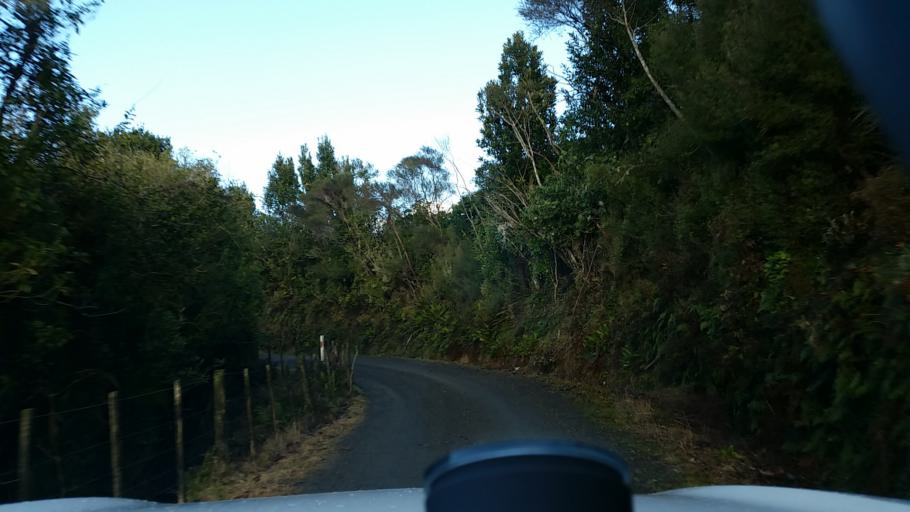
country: NZ
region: Taranaki
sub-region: South Taranaki District
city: Eltham
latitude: -39.4203
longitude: 174.5570
